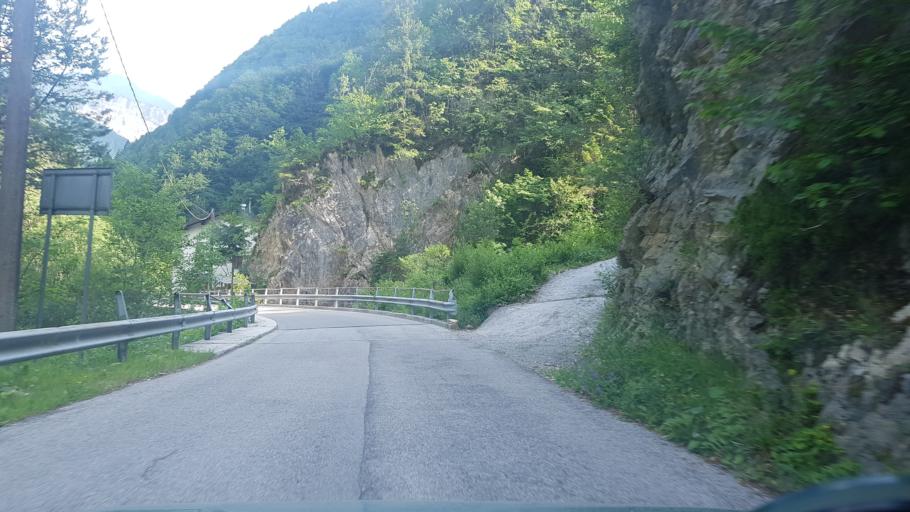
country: IT
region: Friuli Venezia Giulia
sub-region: Provincia di Udine
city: Pontebba
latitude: 46.5161
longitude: 13.2919
